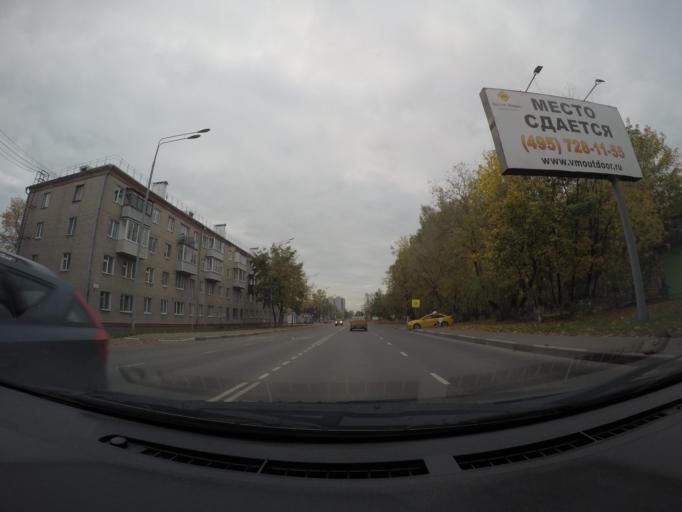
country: RU
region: Moskovskaya
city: Staraya Kupavna
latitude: 55.8082
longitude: 38.1775
